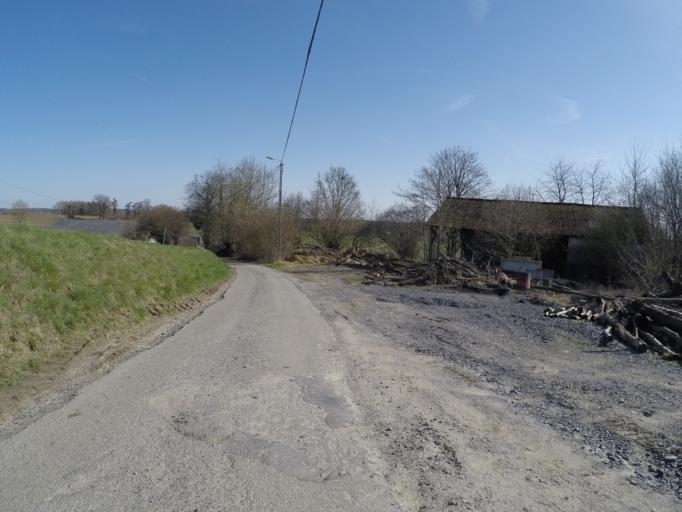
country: BE
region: Wallonia
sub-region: Province de Namur
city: Hamois
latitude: 50.3528
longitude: 5.1075
